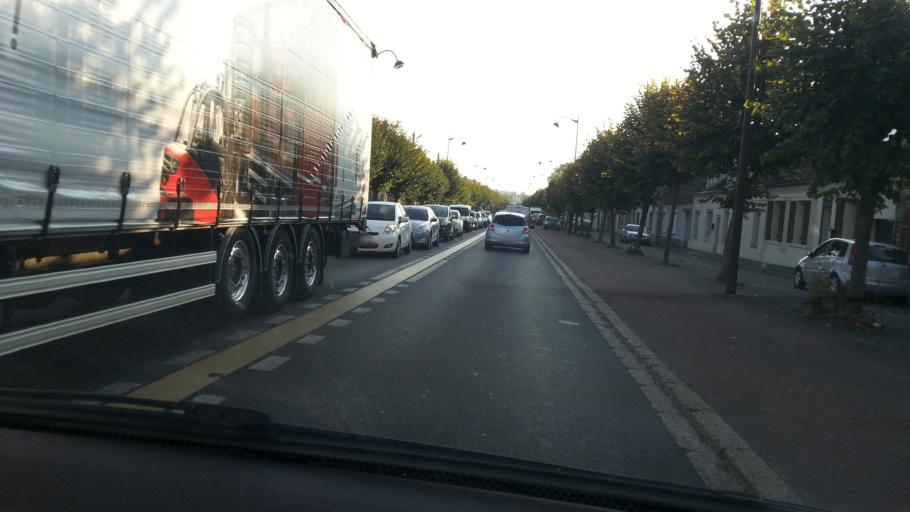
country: FR
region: Picardie
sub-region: Departement de l'Oise
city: Estrees-Saint-Denis
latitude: 49.4307
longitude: 2.6403
